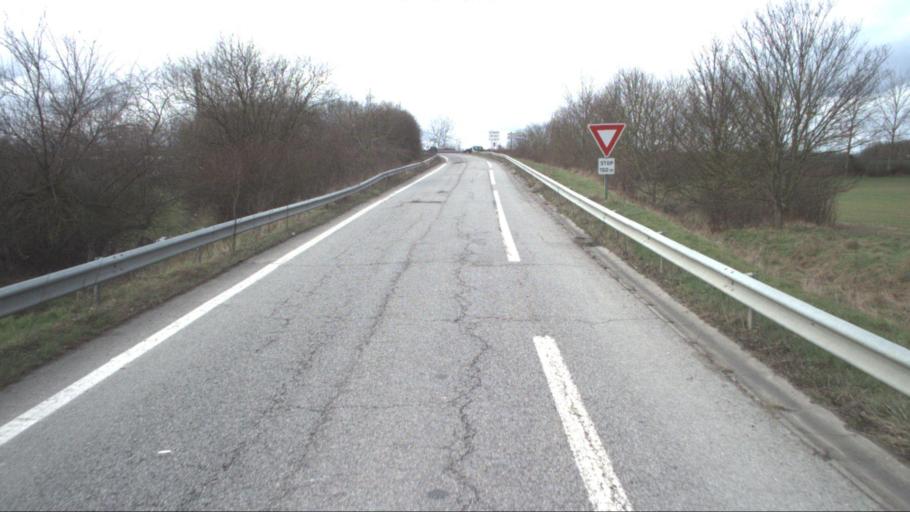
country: FR
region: Ile-de-France
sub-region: Departement des Yvelines
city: Elancourt
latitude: 48.8014
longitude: 1.9521
